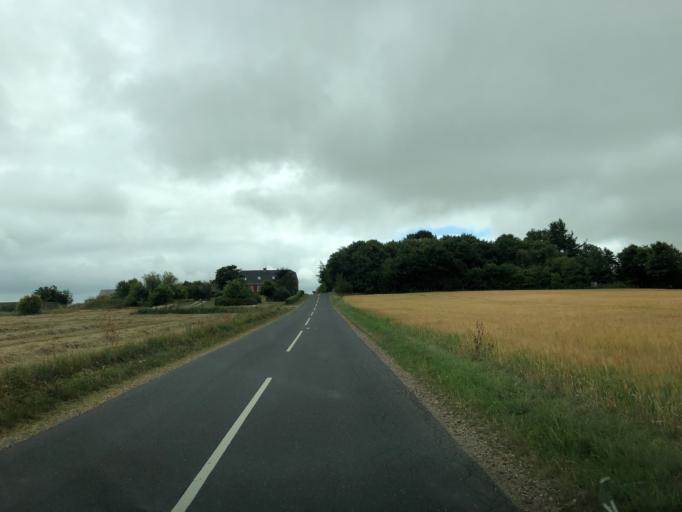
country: DK
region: Central Jutland
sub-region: Ringkobing-Skjern Kommune
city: Videbaek
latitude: 56.2113
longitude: 8.6362
